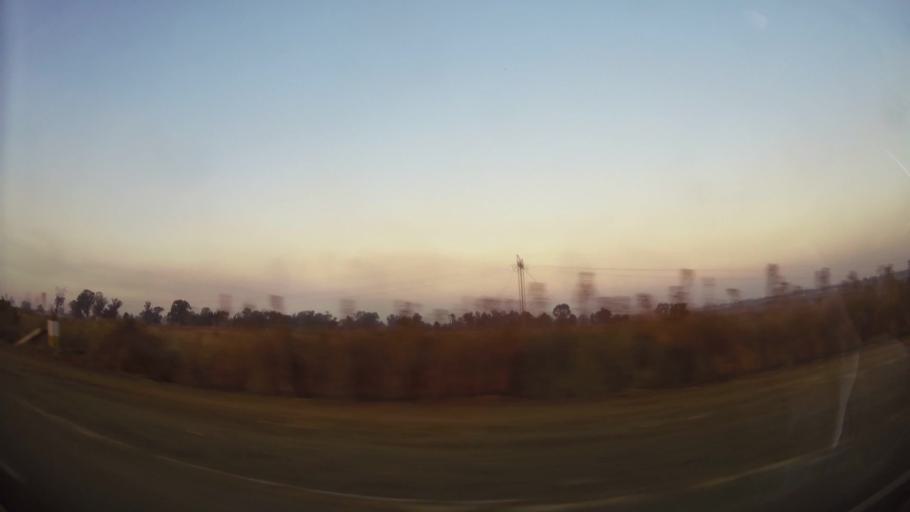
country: ZA
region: Gauteng
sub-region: Ekurhuleni Metropolitan Municipality
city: Springs
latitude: -26.3312
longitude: 28.4231
